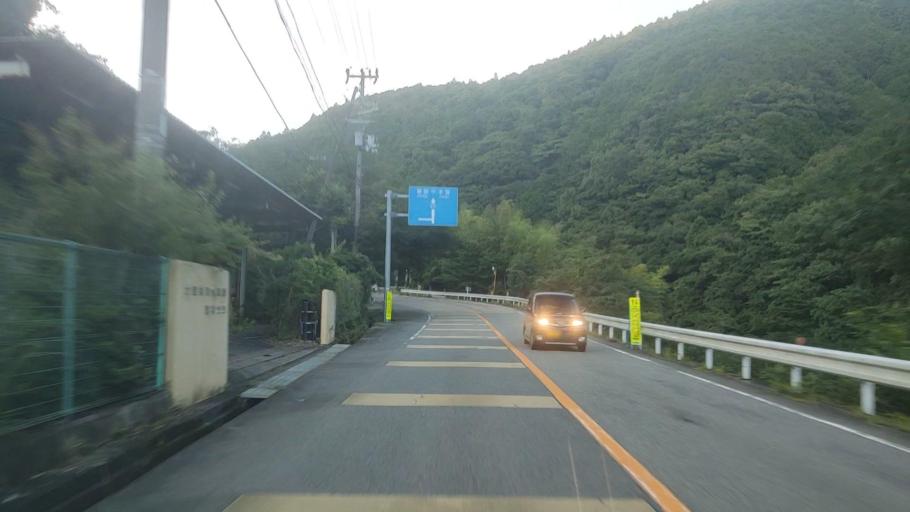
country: JP
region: Wakayama
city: Tanabe
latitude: 33.8148
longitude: 135.5527
